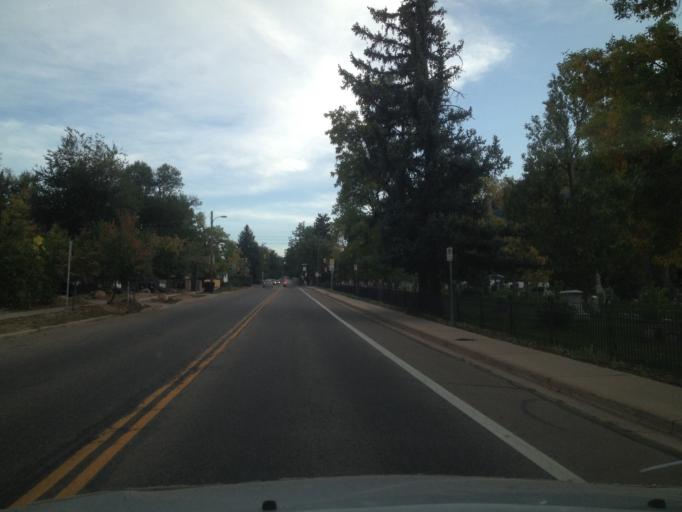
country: US
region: Colorado
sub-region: Boulder County
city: Boulder
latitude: 40.0086
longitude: -105.2820
